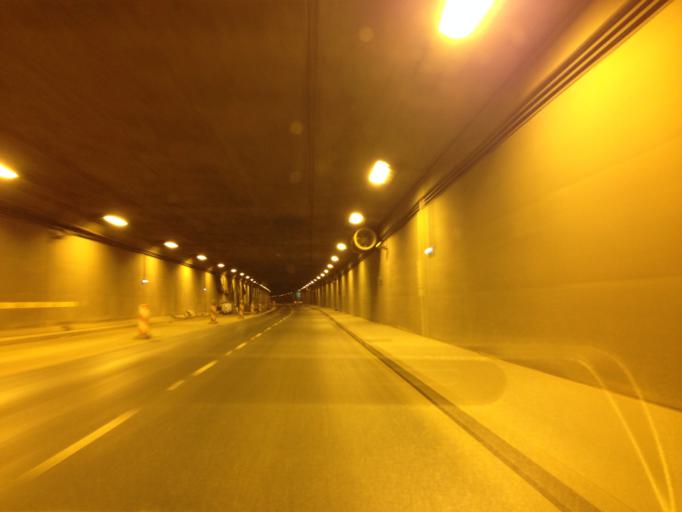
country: PL
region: Masovian Voivodeship
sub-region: Warszawa
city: Praga Polnoc
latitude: 52.2393
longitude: 21.0330
